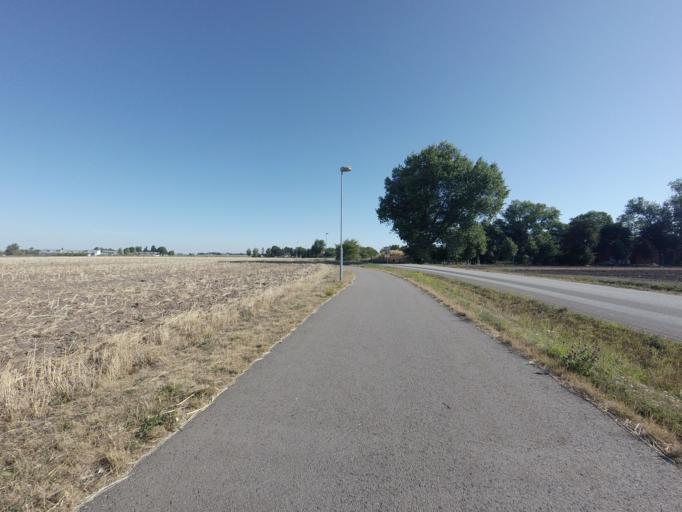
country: SE
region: Skane
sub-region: Trelleborgs Kommun
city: Skare
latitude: 55.4017
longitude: 13.0907
